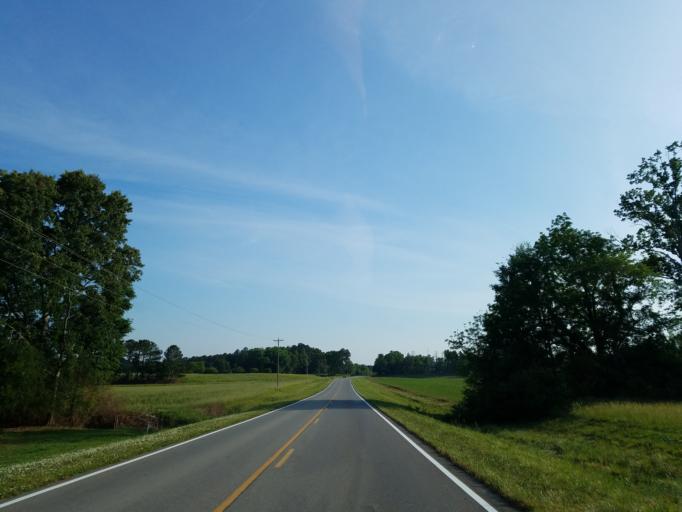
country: US
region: Georgia
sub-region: Chattooga County
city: Trion
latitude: 34.4775
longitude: -85.2622
